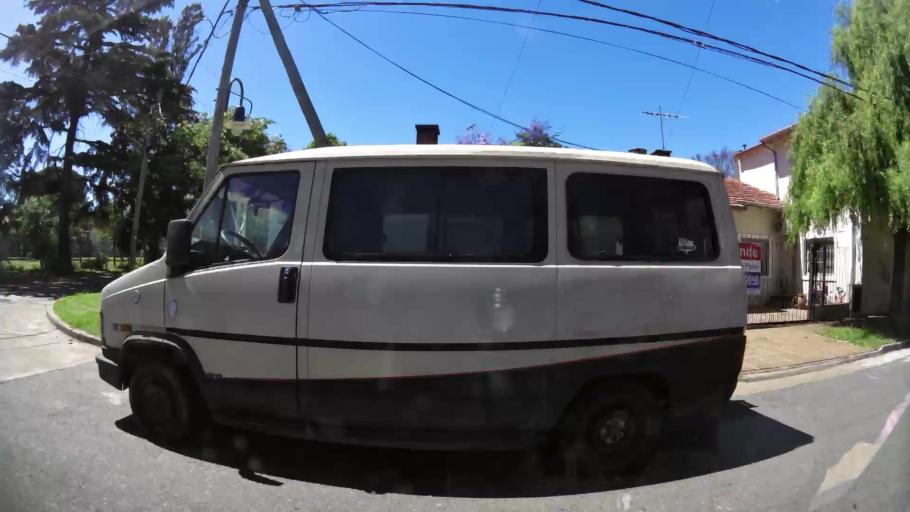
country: AR
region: Buenos Aires
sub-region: Partido de General San Martin
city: General San Martin
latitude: -34.5275
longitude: -58.5421
